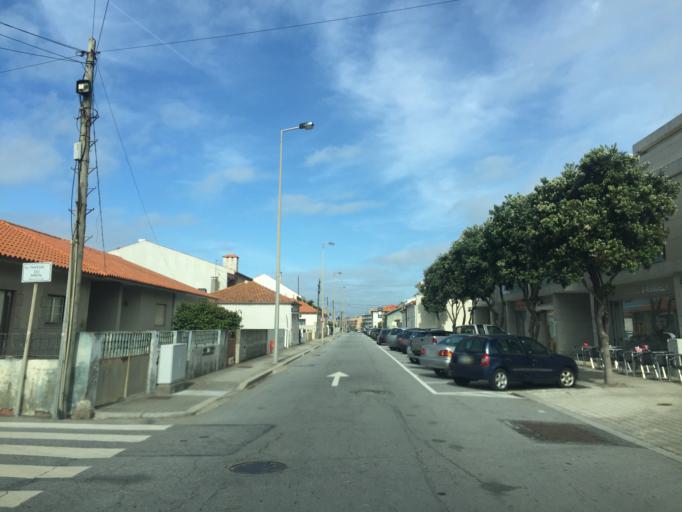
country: PT
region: Porto
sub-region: Matosinhos
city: Lavra
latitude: 41.2407
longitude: -8.7226
